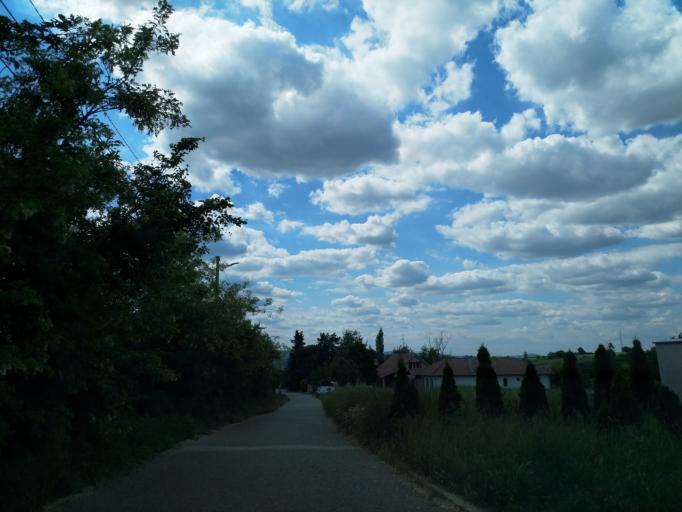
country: RS
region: Central Serbia
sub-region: Pomoravski Okrug
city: Cuprija
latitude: 43.9390
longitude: 21.3127
